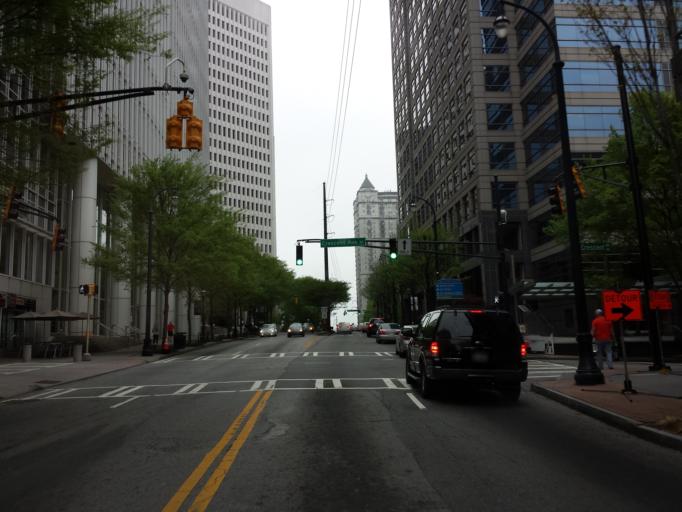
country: US
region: Georgia
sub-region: Fulton County
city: Atlanta
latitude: 33.7866
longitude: -84.3845
